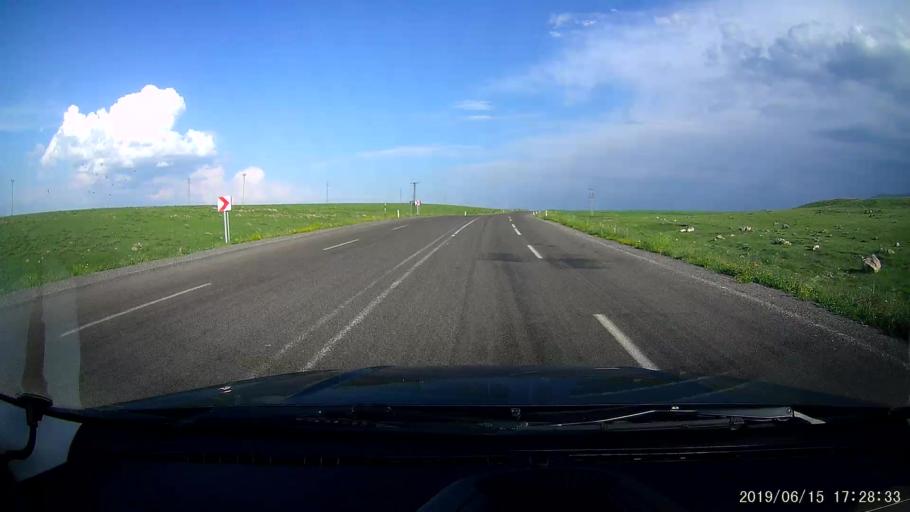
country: TR
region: Kars
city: Basgedikler
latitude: 40.5957
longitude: 43.4443
